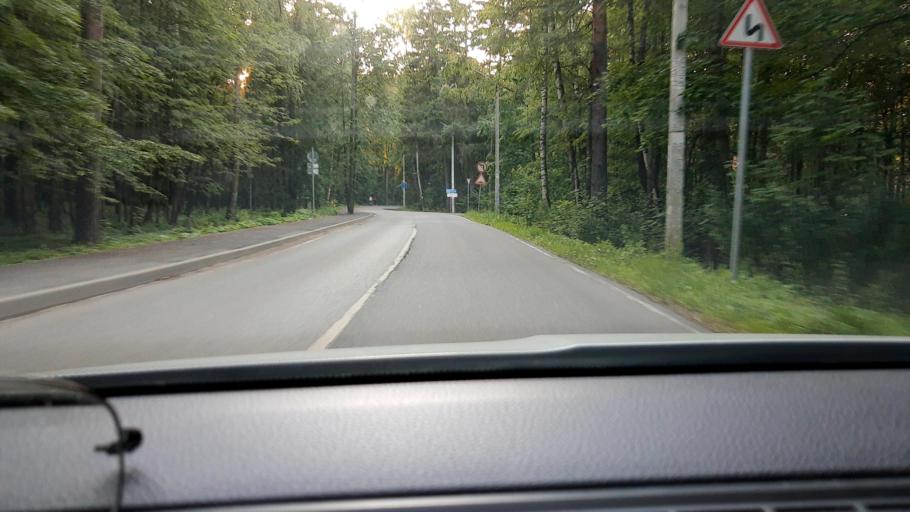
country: RU
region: Moskovskaya
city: Arkhangel'skoye
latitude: 55.7915
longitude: 37.2759
